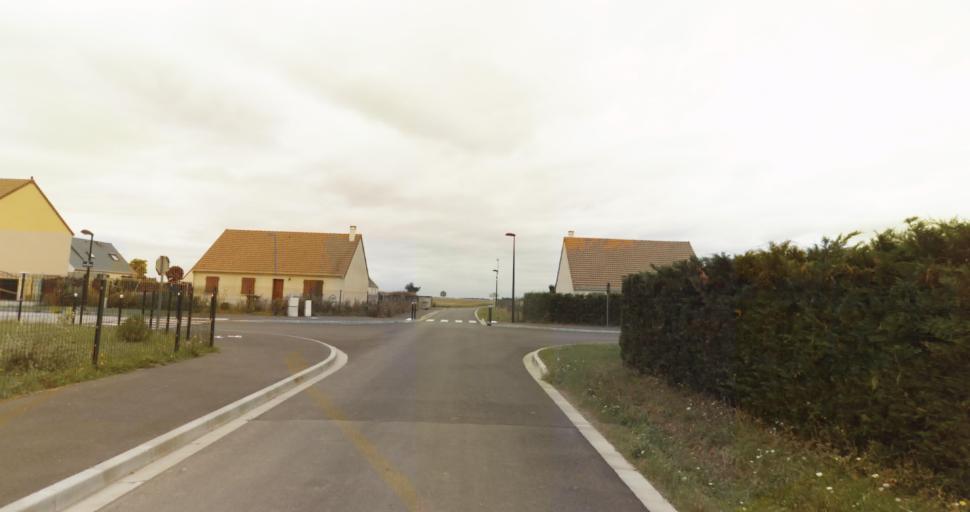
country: FR
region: Haute-Normandie
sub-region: Departement de l'Eure
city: Marcilly-sur-Eure
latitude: 48.9135
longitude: 1.2751
